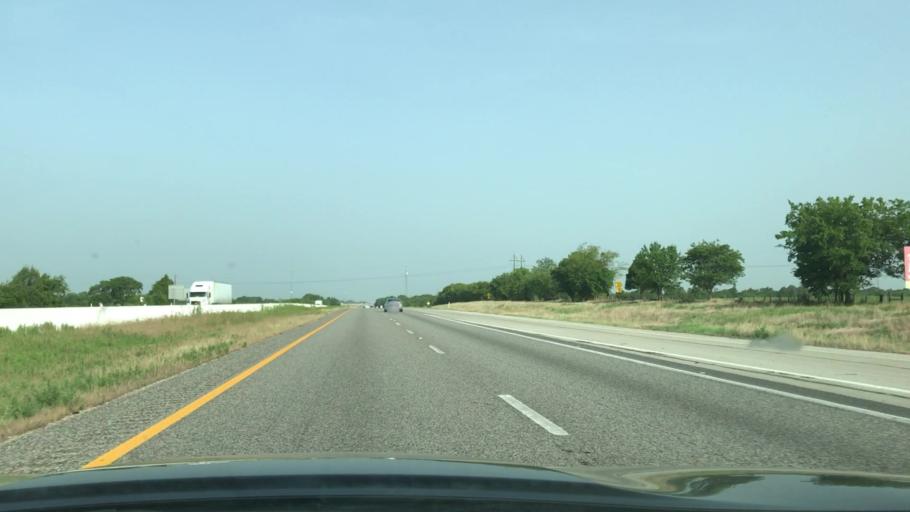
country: US
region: Texas
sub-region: Van Zandt County
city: Wills Point
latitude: 32.6198
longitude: -95.9842
